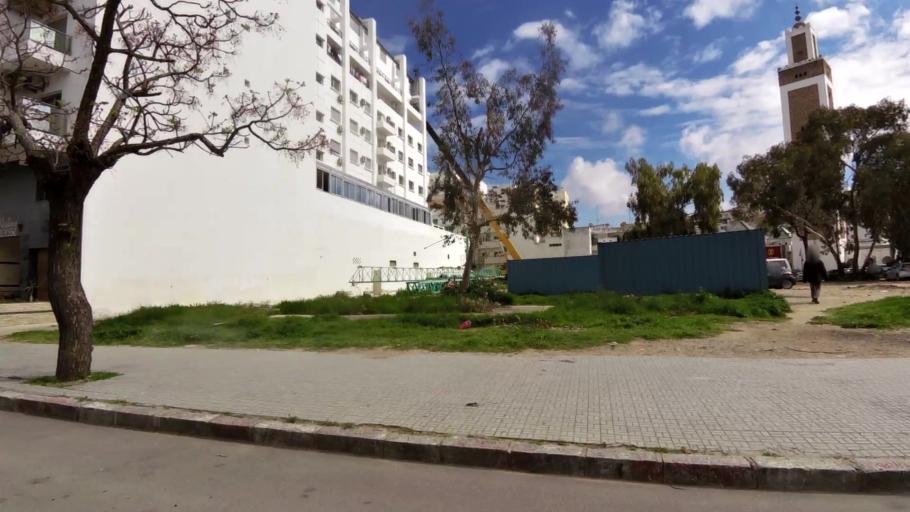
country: MA
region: Tanger-Tetouan
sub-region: Tanger-Assilah
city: Tangier
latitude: 35.7826
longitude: -5.8200
